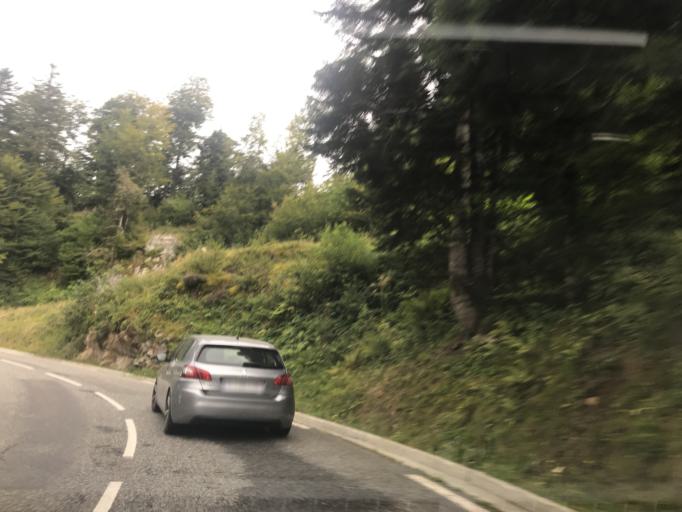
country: ES
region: Catalonia
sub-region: Provincia de Lleida
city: Les
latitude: 42.7701
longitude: 0.6606
